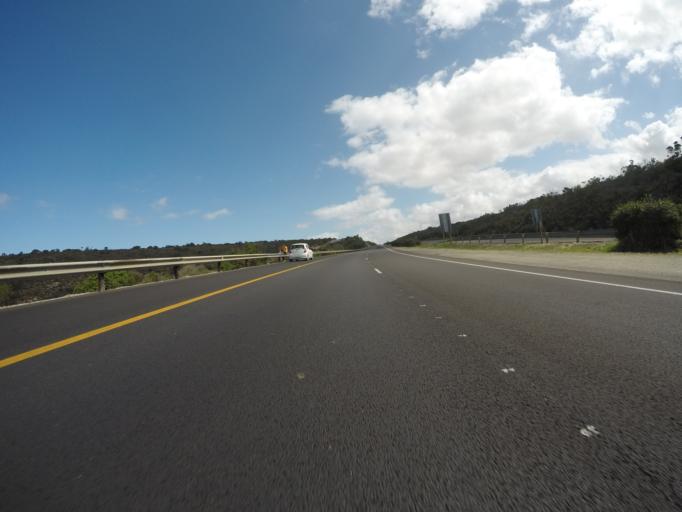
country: ZA
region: Western Cape
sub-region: Eden District Municipality
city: Mossel Bay
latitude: -34.1604
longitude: 22.0980
